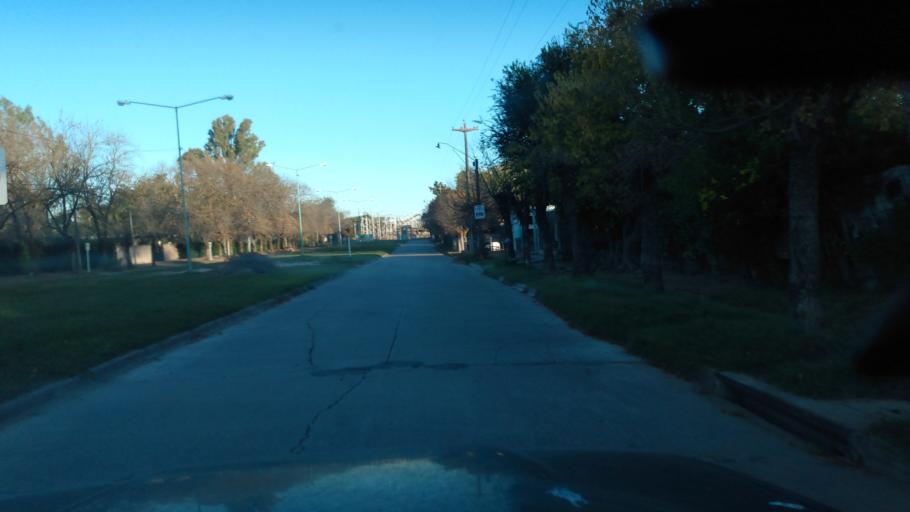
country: AR
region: Buenos Aires
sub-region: Partido de Lujan
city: Lujan
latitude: -34.5623
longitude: -59.1266
